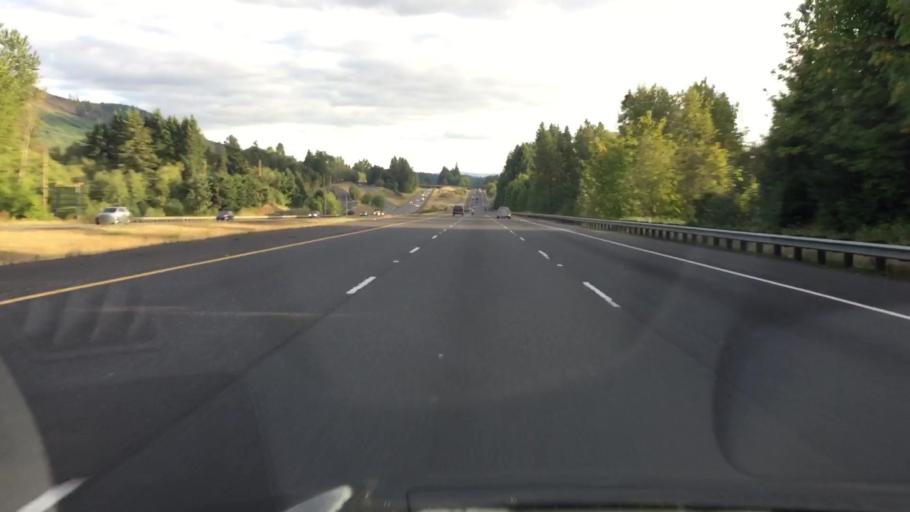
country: US
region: Washington
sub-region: Cowlitz County
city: Castle Rock
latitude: 46.2446
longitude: -122.8857
